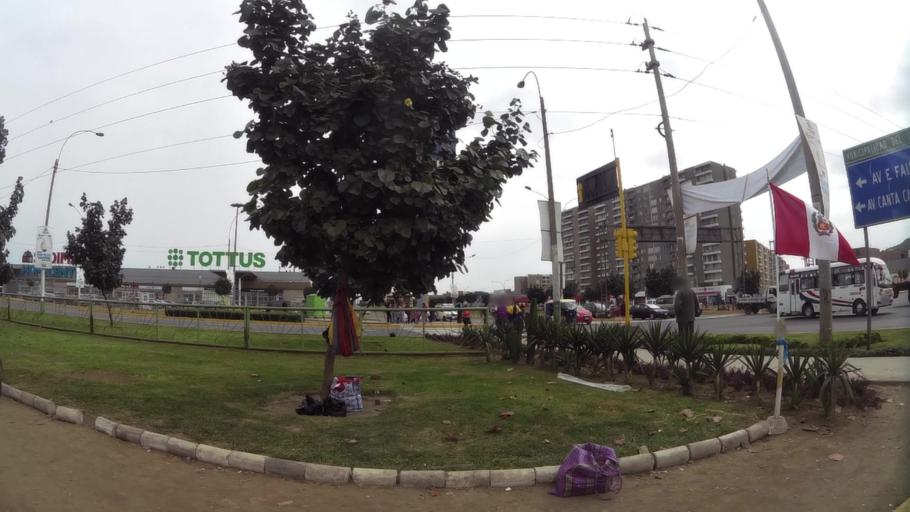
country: PE
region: Callao
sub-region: Callao
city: Callao
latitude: -11.9972
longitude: -77.1125
